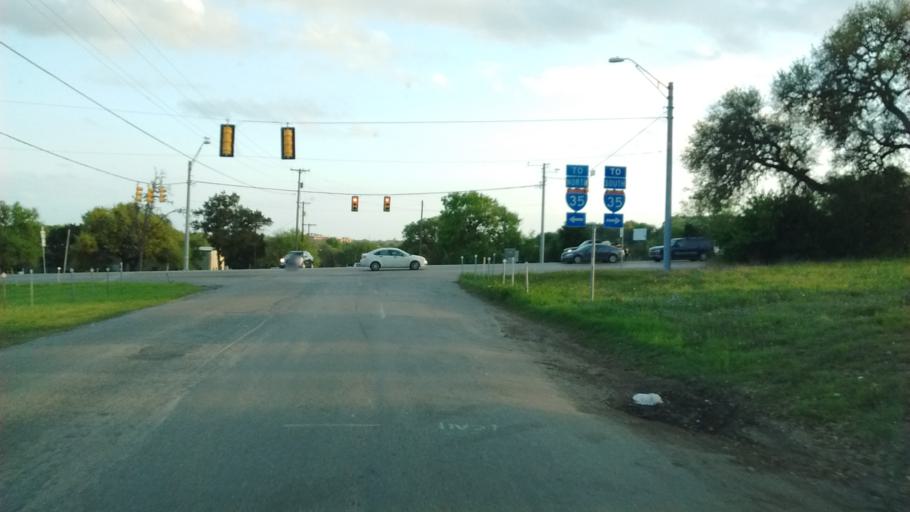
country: US
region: Texas
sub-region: Comal County
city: New Braunfels
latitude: 29.7297
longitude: -98.1256
